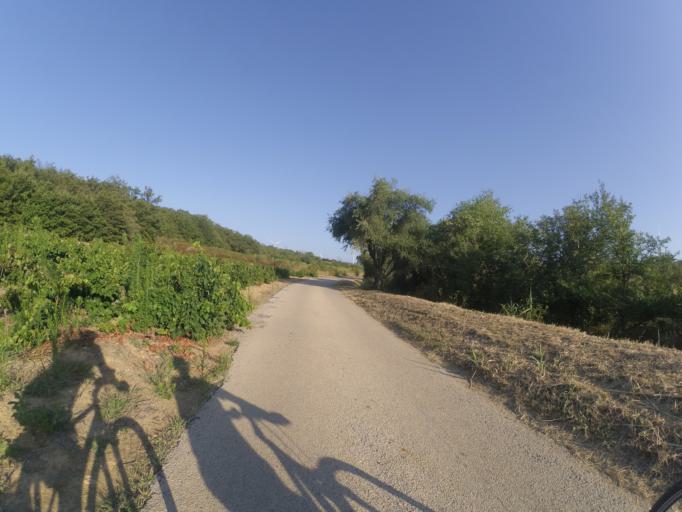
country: FR
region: Languedoc-Roussillon
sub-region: Departement des Pyrenees-Orientales
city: Pezilla-la-Riviere
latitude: 42.7095
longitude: 2.7711
